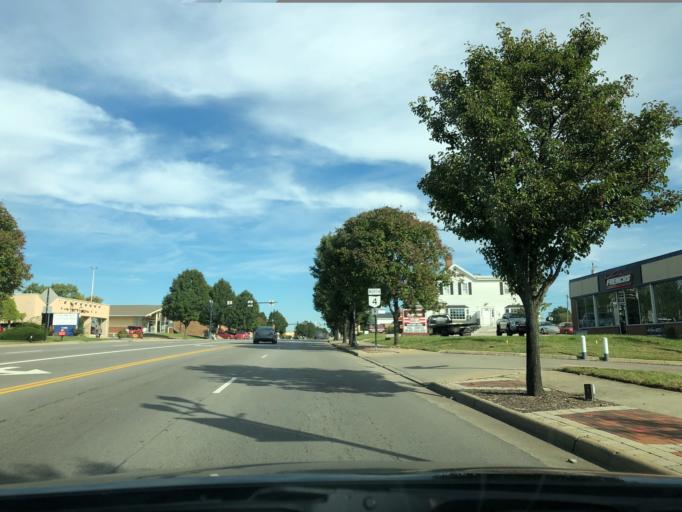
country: US
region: Ohio
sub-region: Hamilton County
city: Springdale
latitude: 39.2827
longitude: -84.4855
